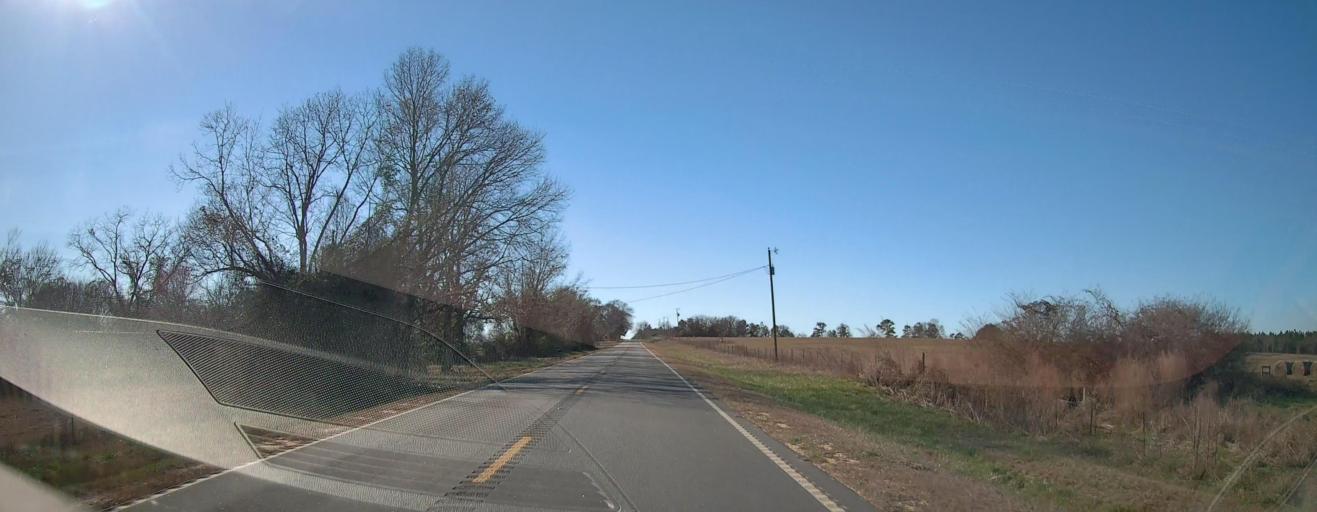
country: US
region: Georgia
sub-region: Taylor County
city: Butler
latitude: 32.6598
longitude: -84.3347
